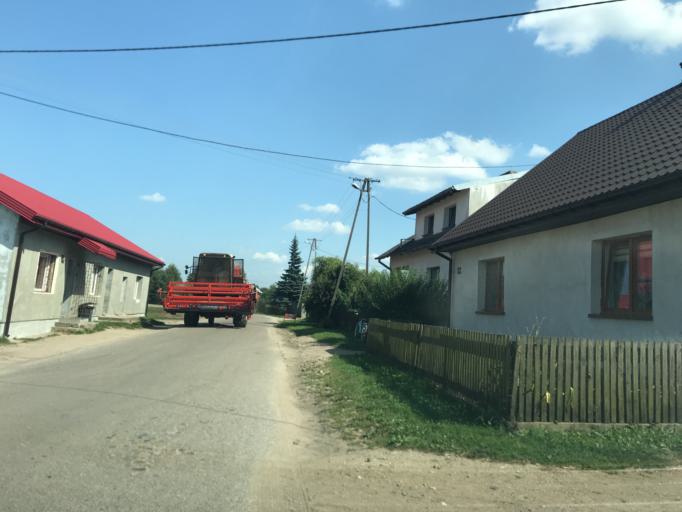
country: PL
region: Masovian Voivodeship
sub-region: Powiat zurominski
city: Lubowidz
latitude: 53.1730
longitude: 19.8971
